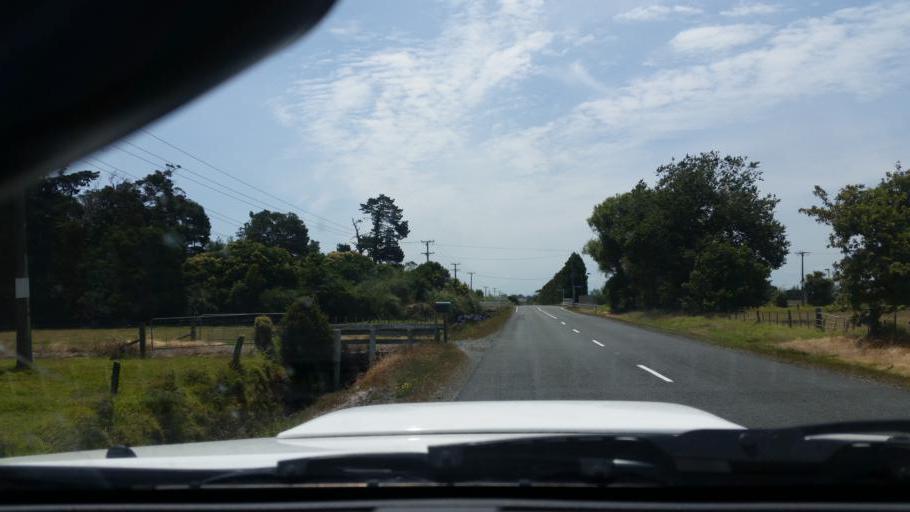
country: NZ
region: Northland
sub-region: Kaipara District
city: Dargaville
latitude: -36.0607
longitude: 173.9360
